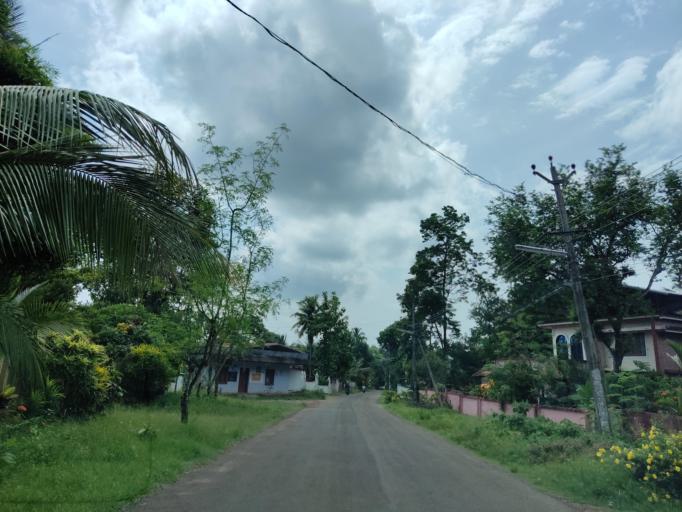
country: IN
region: Kerala
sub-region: Alappuzha
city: Mavelikara
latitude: 9.2537
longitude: 76.5680
